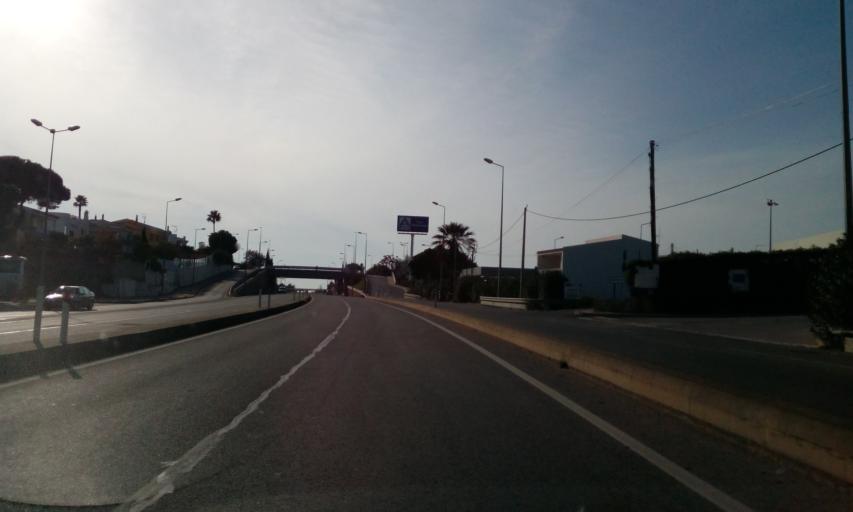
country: PT
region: Faro
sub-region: Faro
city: Faro
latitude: 37.0364
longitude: -7.9583
